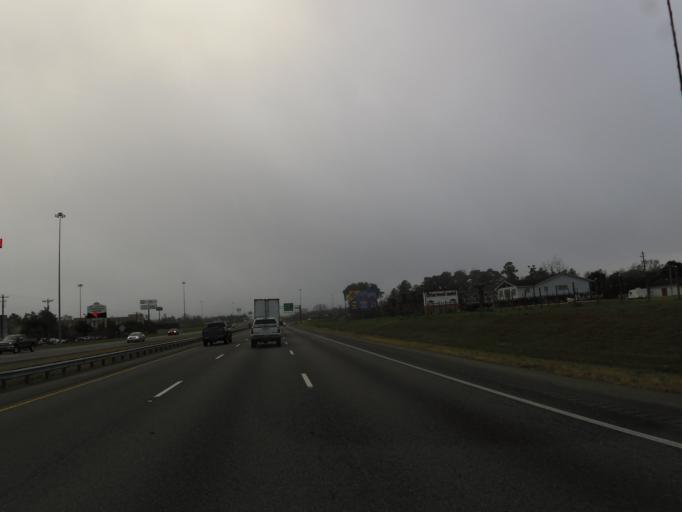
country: US
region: Georgia
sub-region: Lowndes County
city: Remerton
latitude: 30.8239
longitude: -83.3204
